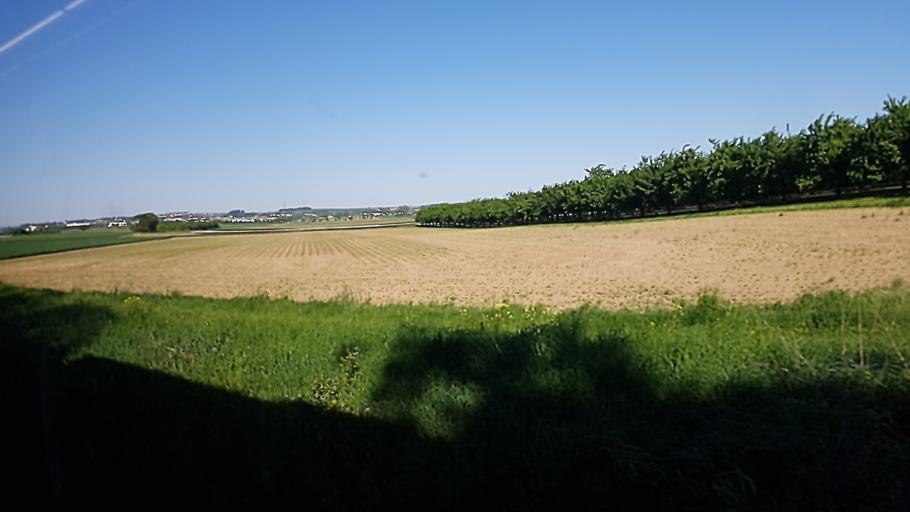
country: DE
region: Rheinland-Pfalz
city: Klein-Winternheim
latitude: 49.9497
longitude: 8.2277
